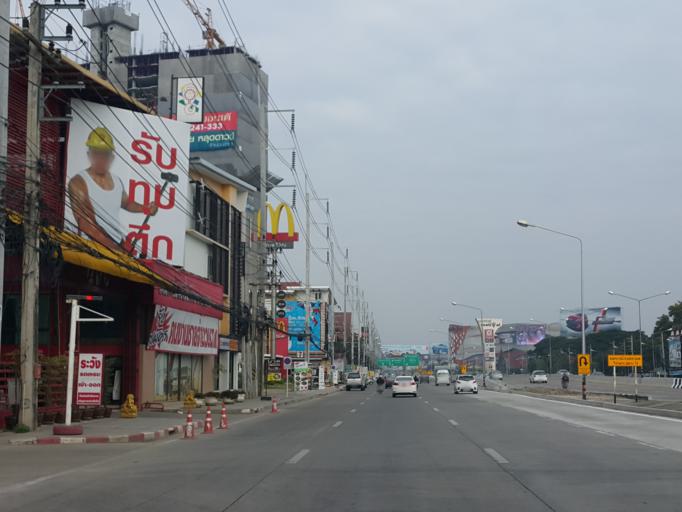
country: TH
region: Chiang Mai
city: Chiang Mai
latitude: 18.7994
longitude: 99.0199
